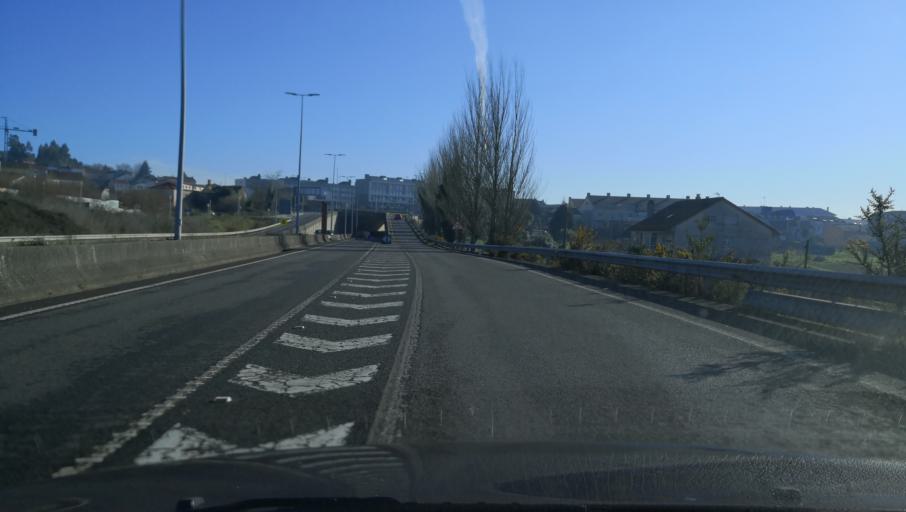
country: ES
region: Galicia
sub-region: Provincia da Coruna
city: Santiago de Compostela
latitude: 42.8594
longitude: -8.5435
